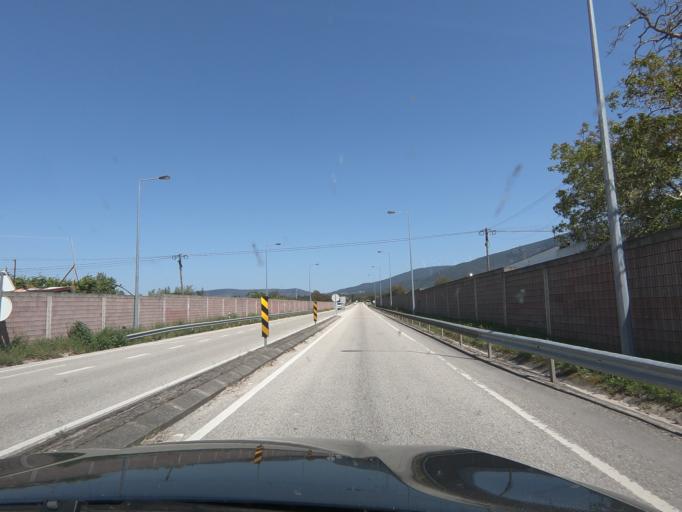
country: PT
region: Coimbra
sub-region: Lousa
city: Lousa
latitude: 40.1283
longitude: -8.2652
